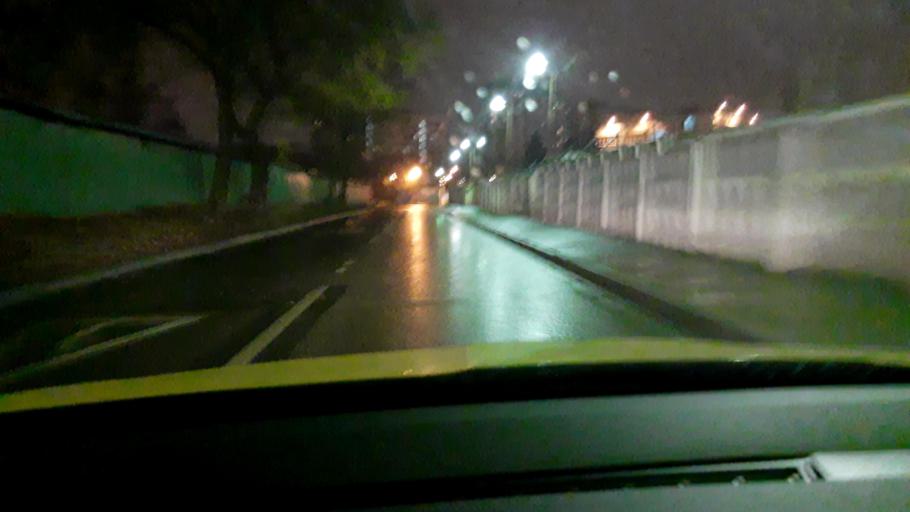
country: RU
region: Moscow
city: Kozeyevo
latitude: 55.8948
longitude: 37.6449
